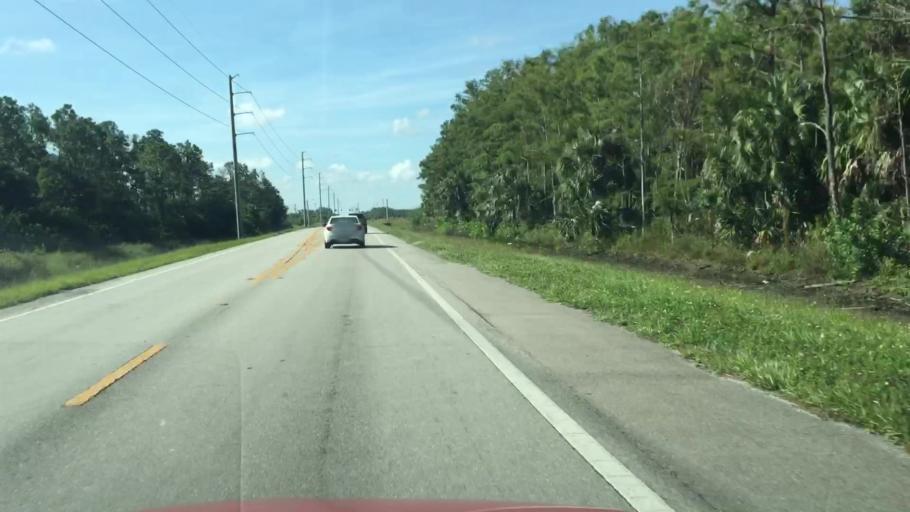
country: US
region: Florida
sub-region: Collier County
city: Orangetree
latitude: 26.3304
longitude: -81.5950
